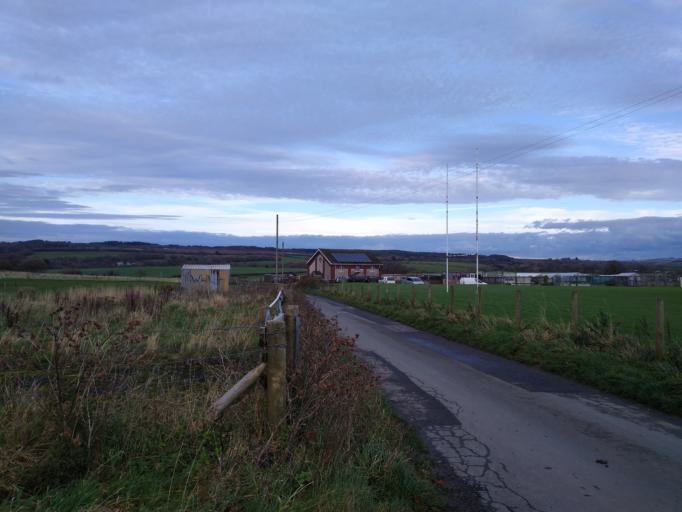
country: GB
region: England
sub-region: Cumbria
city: Flimby
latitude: 54.6547
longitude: -3.4890
